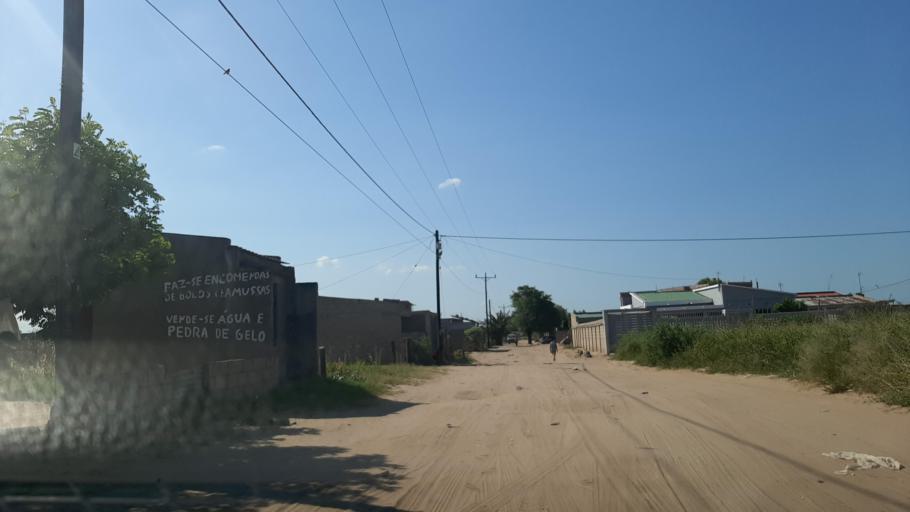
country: MZ
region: Maputo
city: Matola
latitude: -25.8077
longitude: 32.4916
